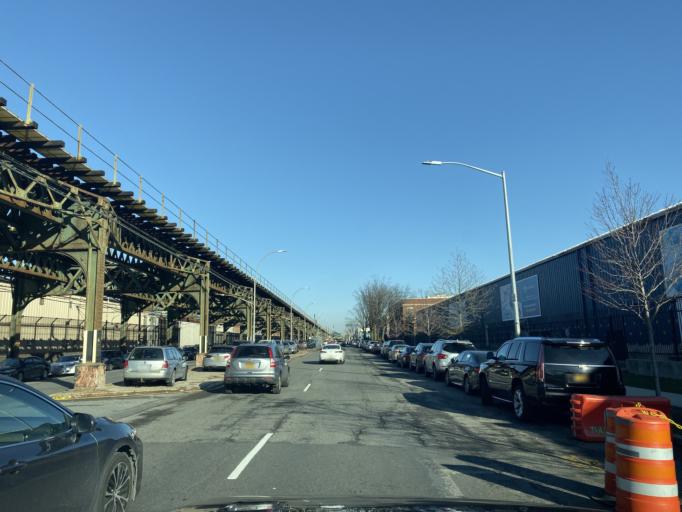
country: US
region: New York
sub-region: Kings County
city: Coney Island
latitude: 40.5843
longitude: -73.9744
